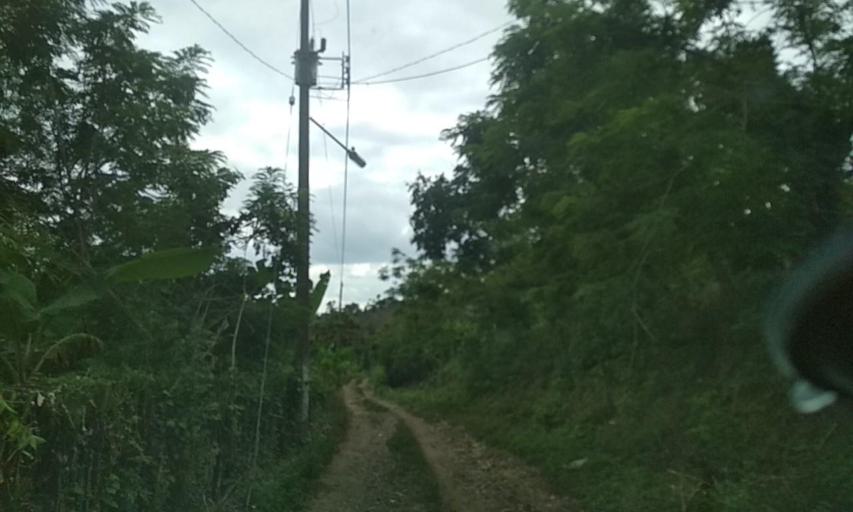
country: MX
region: Veracruz
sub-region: Papantla
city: Polutla
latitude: 20.5898
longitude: -97.2783
